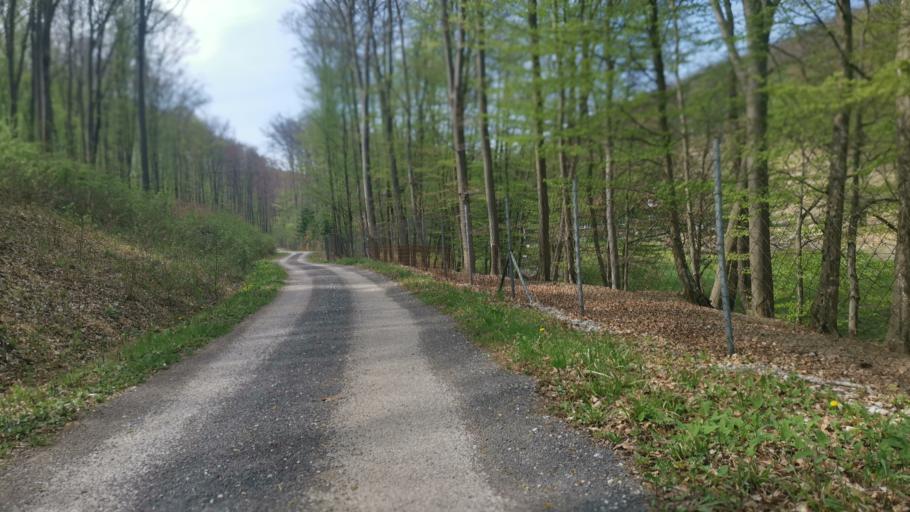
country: SK
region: Trnavsky
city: Smolenice
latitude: 48.5540
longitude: 17.4513
